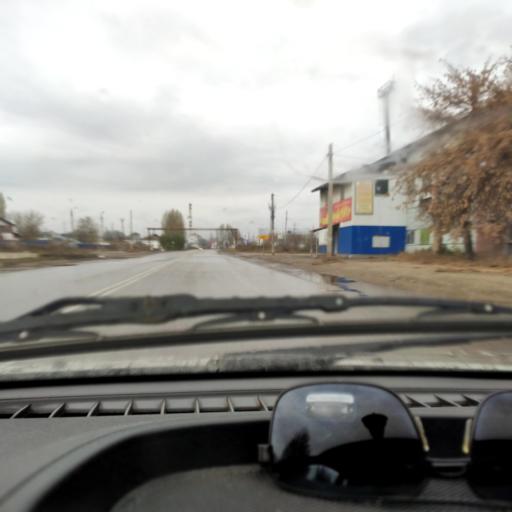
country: RU
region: Samara
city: Tol'yatti
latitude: 53.5250
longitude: 49.4711
